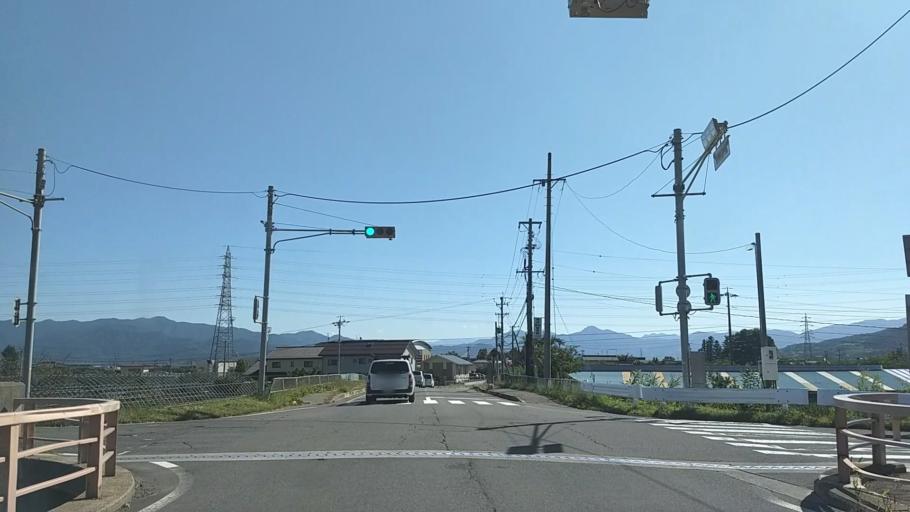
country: JP
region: Nagano
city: Nagano-shi
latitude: 36.6192
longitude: 138.1417
